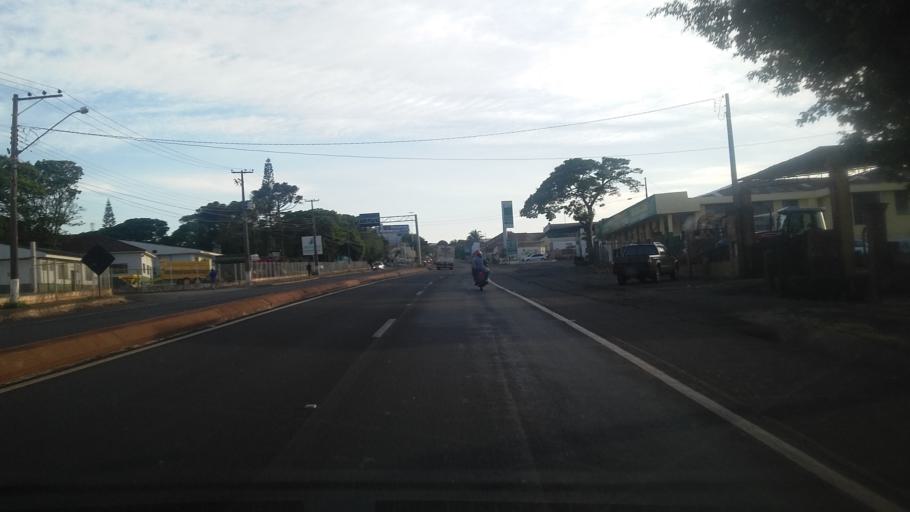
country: BR
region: Parana
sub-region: Assai
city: Assai
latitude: -23.1957
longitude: -50.6534
